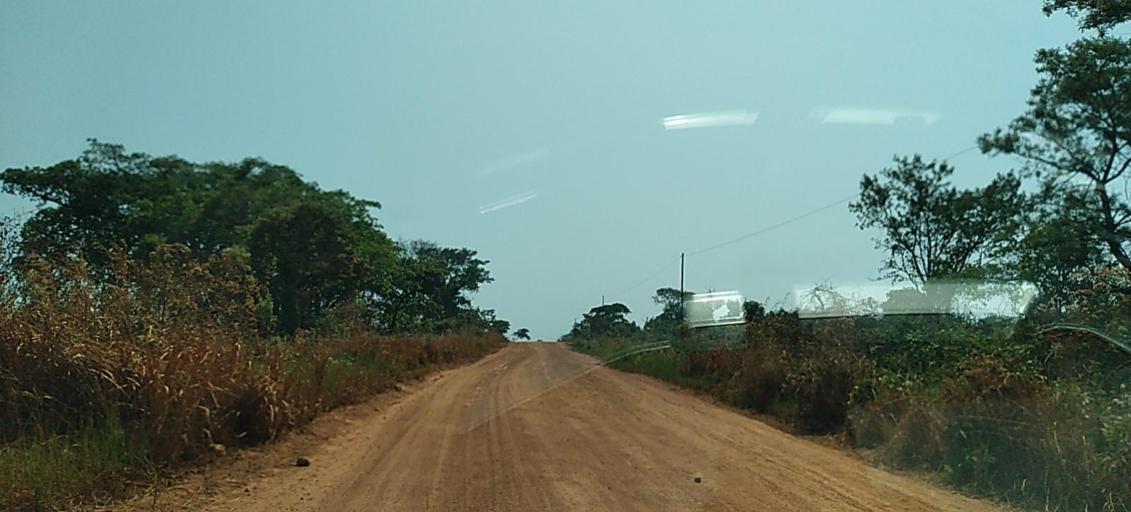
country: ZM
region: North-Western
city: Kansanshi
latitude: -12.0056
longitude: 26.5815
